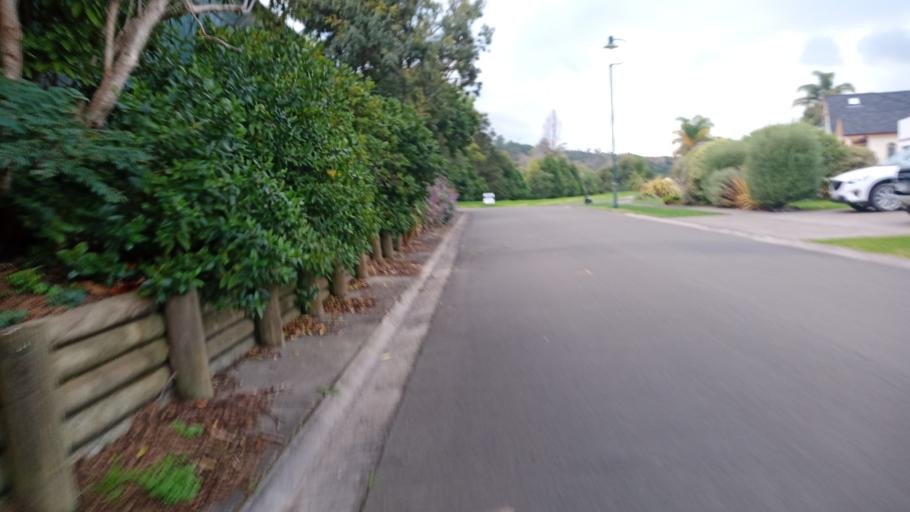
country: NZ
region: Gisborne
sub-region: Gisborne District
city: Gisborne
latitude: -38.6420
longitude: 178.0180
